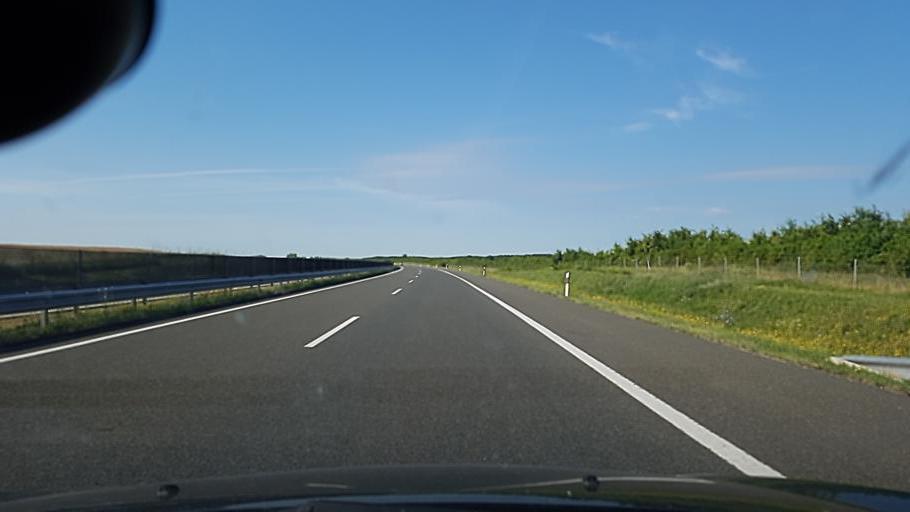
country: HU
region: Fejer
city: Baracs
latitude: 46.8960
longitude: 18.8781
